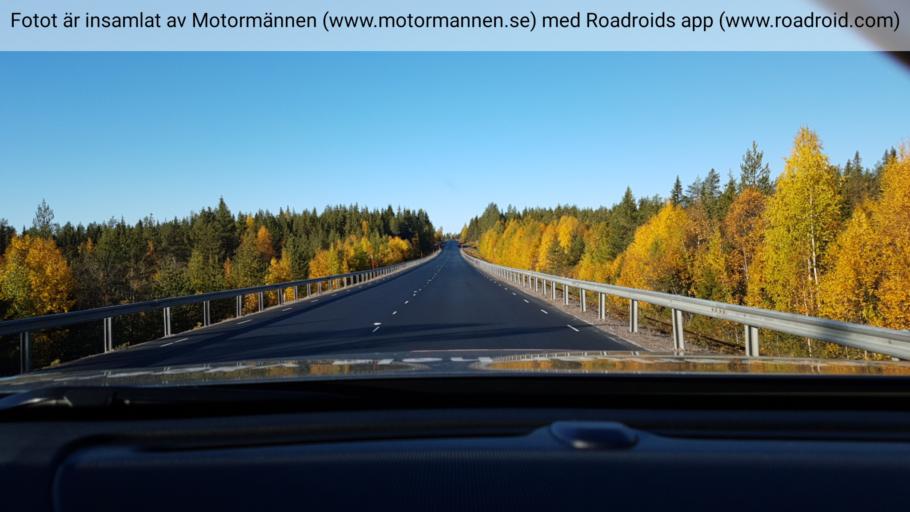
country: SE
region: Vaesterbotten
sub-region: Norsjo Kommun
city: Norsjoe
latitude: 65.4118
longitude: 19.8125
